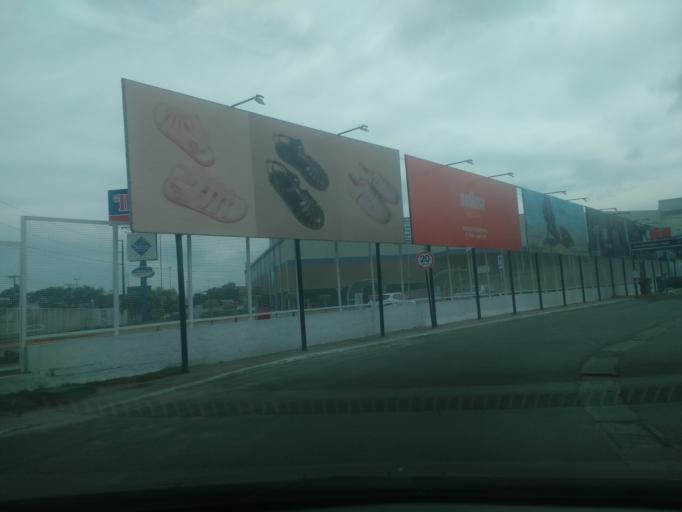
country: BR
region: Alagoas
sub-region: Maceio
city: Maceio
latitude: -9.6498
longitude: -35.7152
